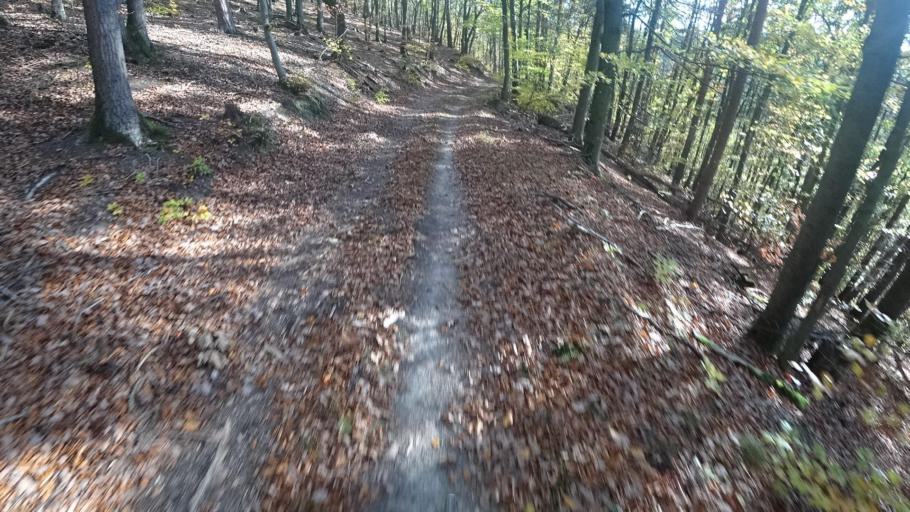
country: DE
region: Rheinland-Pfalz
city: Lind
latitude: 50.5151
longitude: 6.9442
